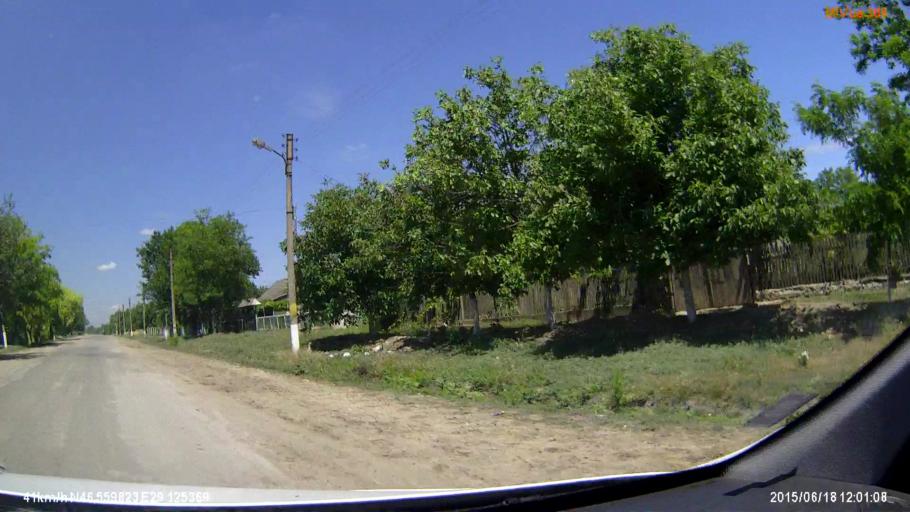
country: UA
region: Odessa
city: Serpneve
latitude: 46.5596
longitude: 29.1255
